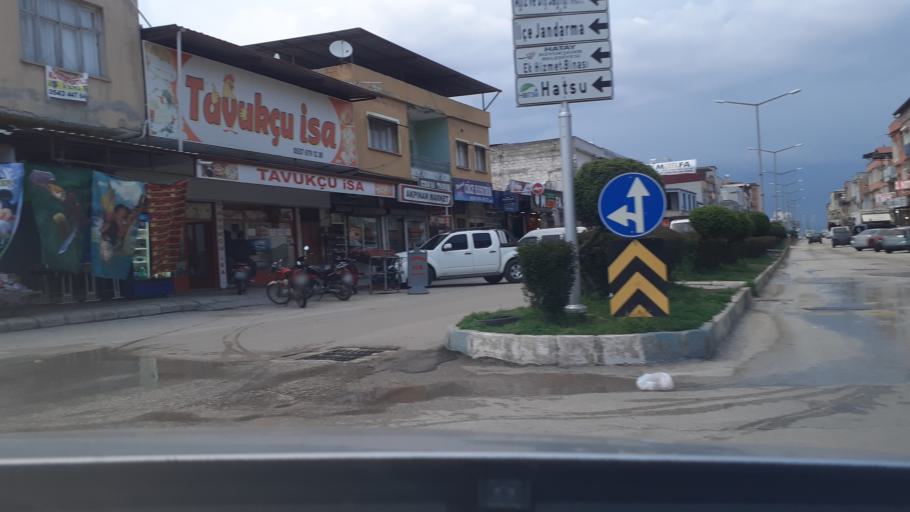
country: TR
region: Hatay
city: Kirikhan
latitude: 36.4967
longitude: 36.3607
